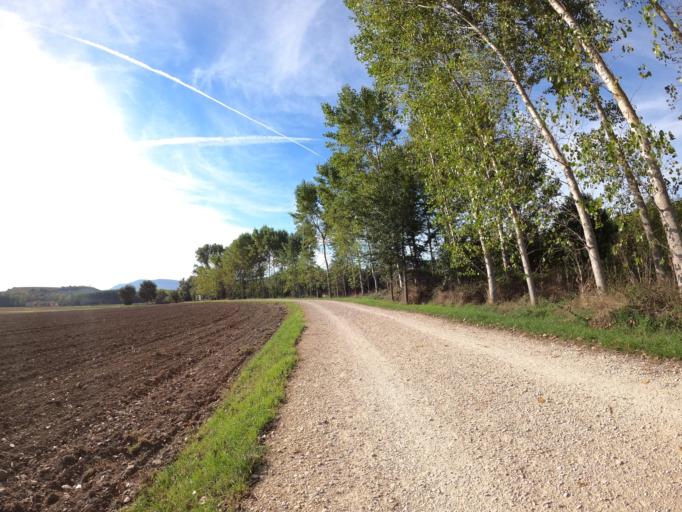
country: ES
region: Navarre
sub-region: Provincia de Navarra
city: Oltza
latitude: 42.8041
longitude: -1.7689
